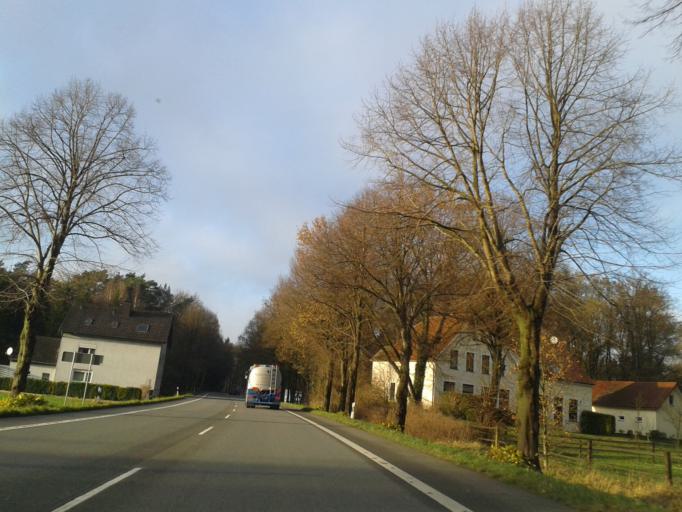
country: DE
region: North Rhine-Westphalia
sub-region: Regierungsbezirk Detmold
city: Augustdorf
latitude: 51.8938
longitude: 8.6731
